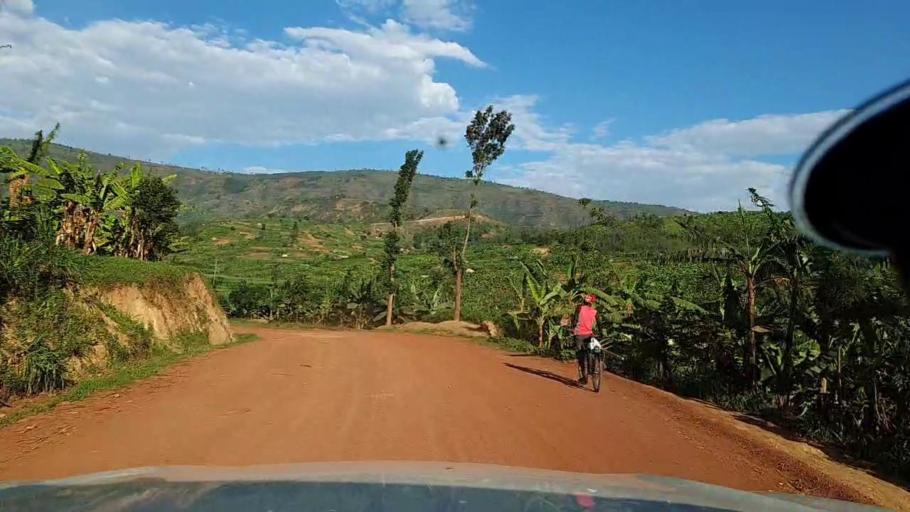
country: RW
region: Kigali
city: Kigali
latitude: -1.8654
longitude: 29.9268
